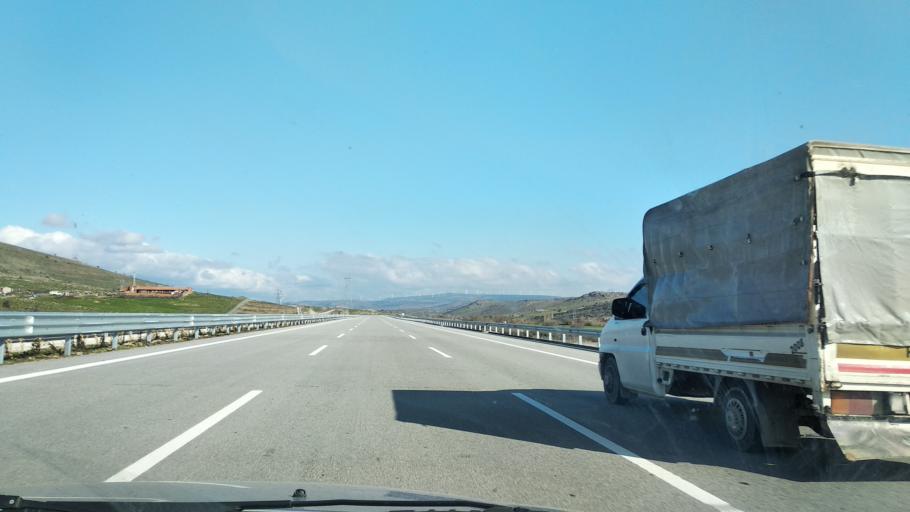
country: TR
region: Izmir
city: Yenisakran
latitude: 38.8276
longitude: 27.0369
